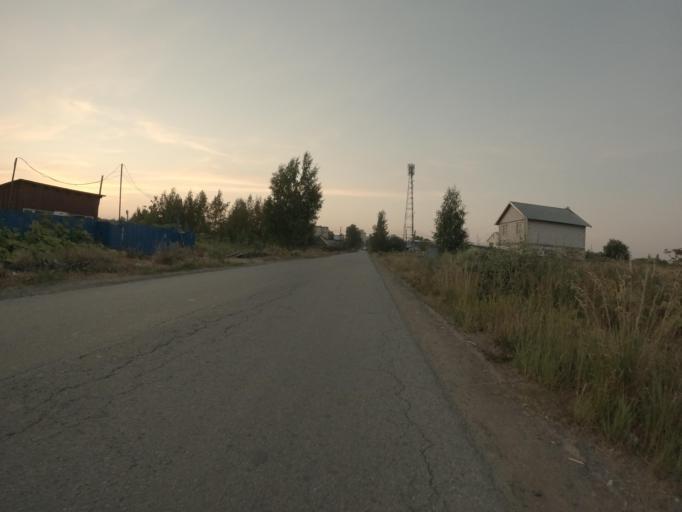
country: RU
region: Leningrad
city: Yanino Vtoroye
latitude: 59.9439
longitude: 30.5542
